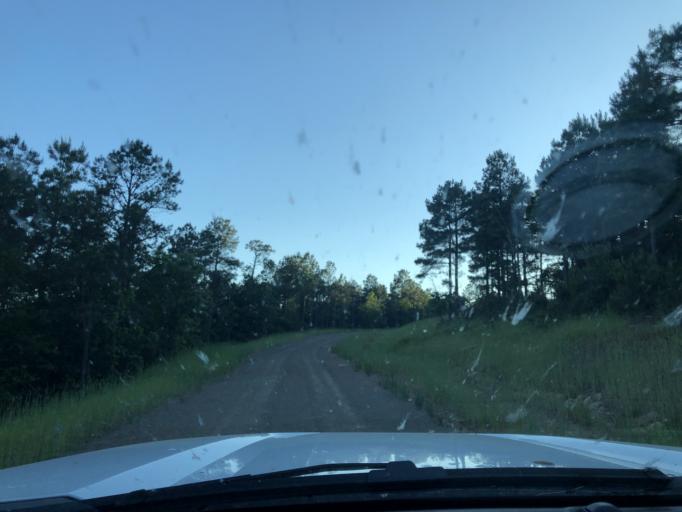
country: US
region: Oklahoma
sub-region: Le Flore County
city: Talihina
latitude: 34.5798
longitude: -95.1710
